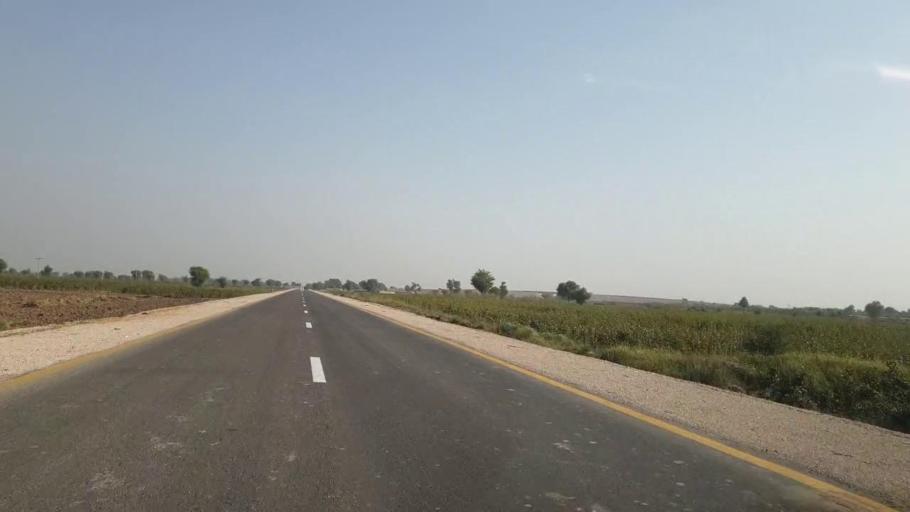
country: PK
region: Sindh
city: Sehwan
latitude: 26.4632
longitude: 67.8001
